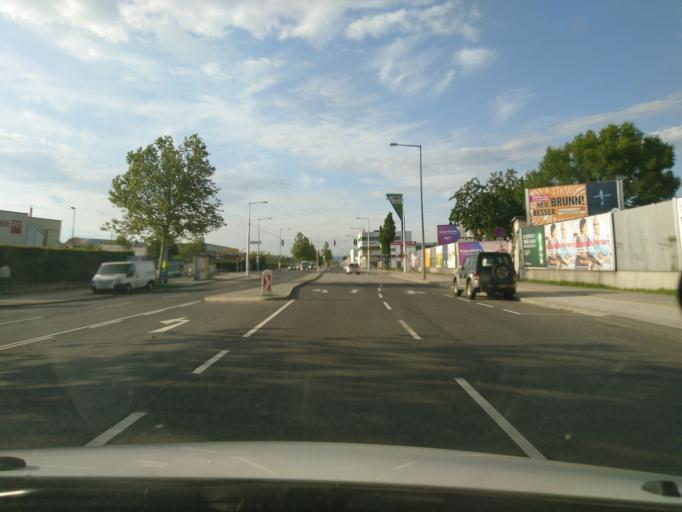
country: AT
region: Lower Austria
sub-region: Politischer Bezirk Modling
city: Brunn am Gebirge
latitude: 48.1322
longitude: 16.2980
